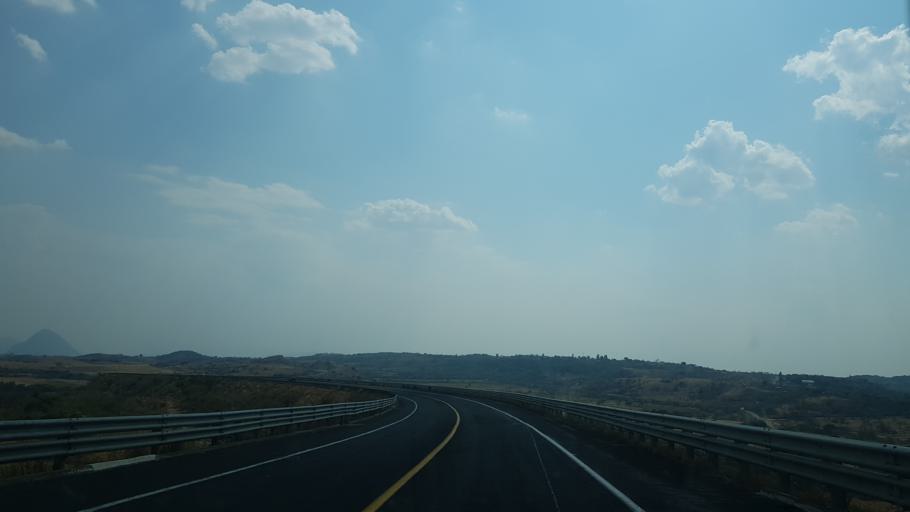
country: MX
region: Puebla
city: San Juan Amecac
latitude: 18.8192
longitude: -98.6929
